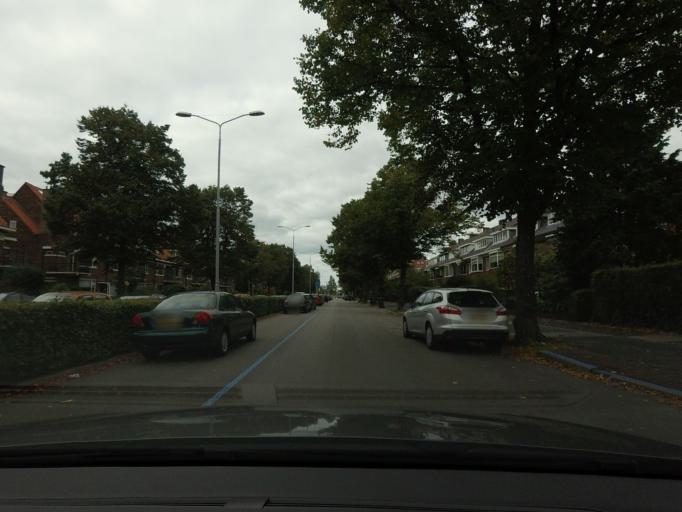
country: NL
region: South Holland
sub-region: Gemeente Leidschendam-Voorburg
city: Voorburg
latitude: 52.0766
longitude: 4.3483
